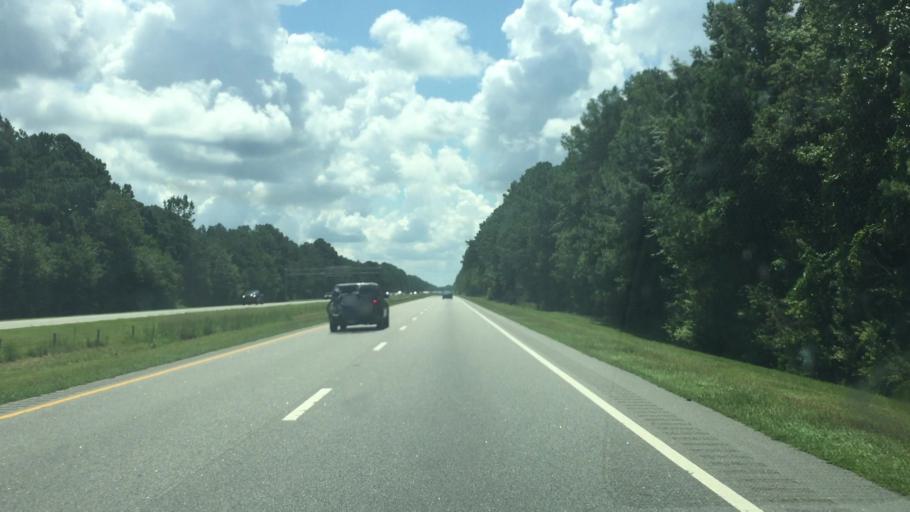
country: US
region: North Carolina
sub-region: Robeson County
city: Lumberton
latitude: 34.5601
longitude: -79.0267
